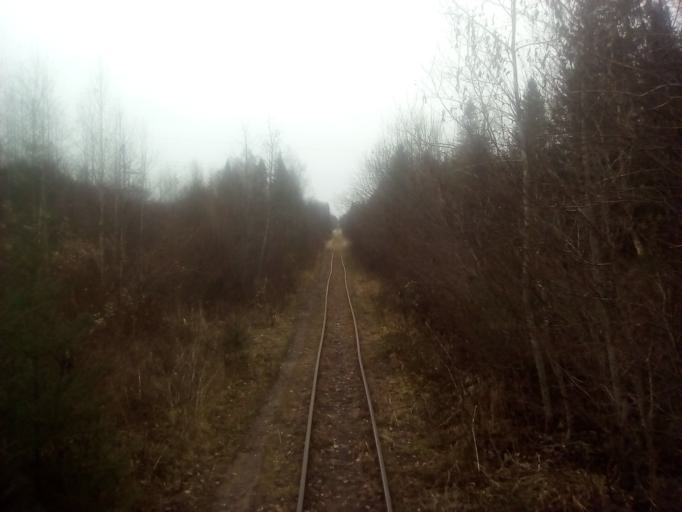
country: RU
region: Vologda
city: Kharovsk
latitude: 59.8089
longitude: 40.2224
